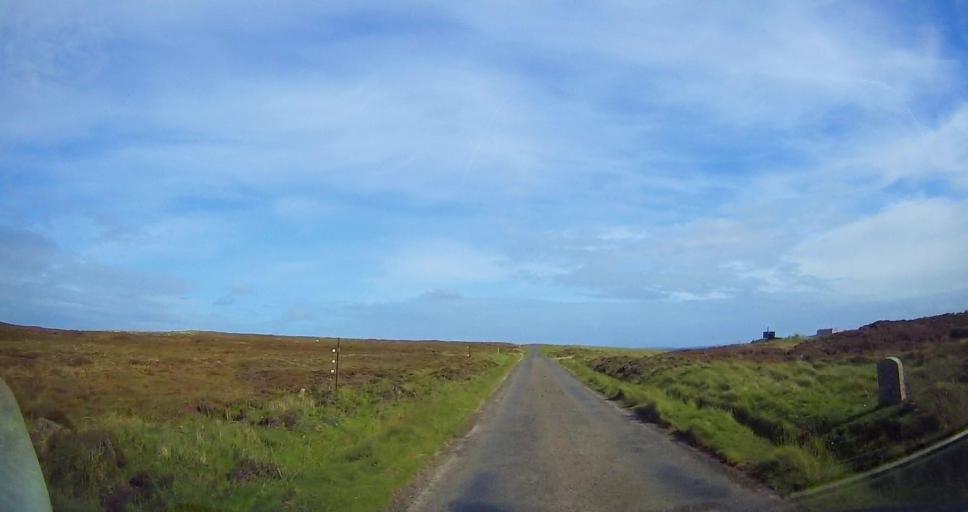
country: GB
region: Scotland
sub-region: Orkney Islands
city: Stromness
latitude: 58.8545
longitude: -3.2107
